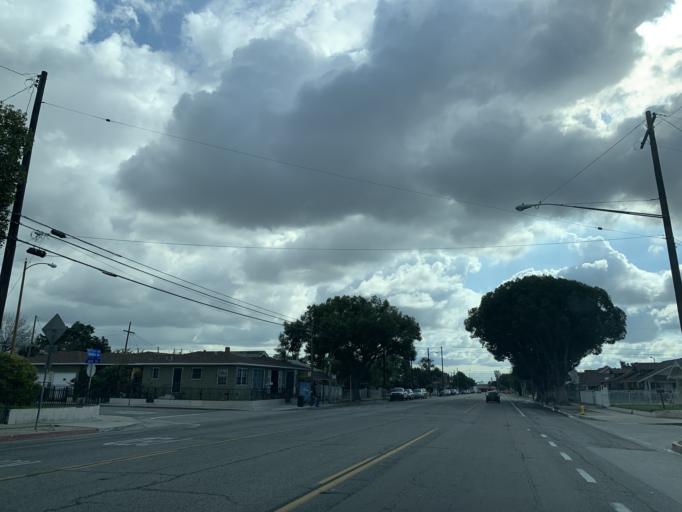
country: US
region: California
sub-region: Los Angeles County
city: Florence-Graham
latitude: 33.9784
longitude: -118.2412
